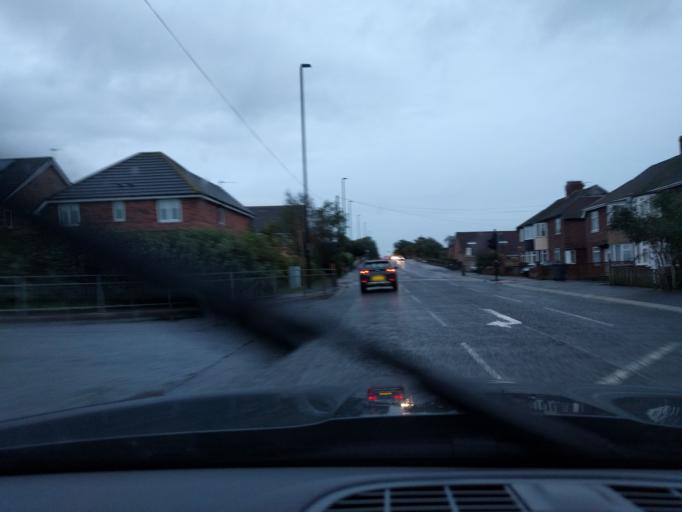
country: GB
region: England
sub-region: Northumberland
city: Backworth
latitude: 55.0244
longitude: -1.5435
